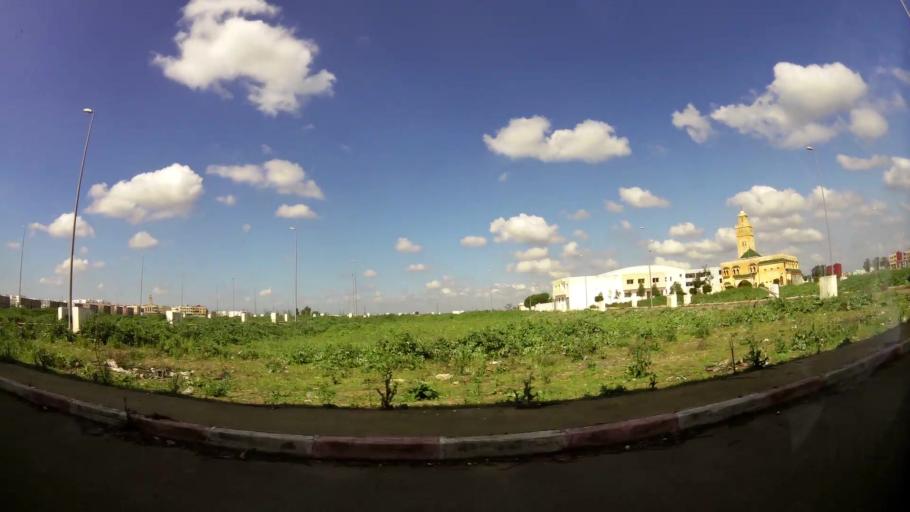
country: MA
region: Grand Casablanca
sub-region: Mediouna
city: Mediouna
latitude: 33.4493
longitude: -7.5068
